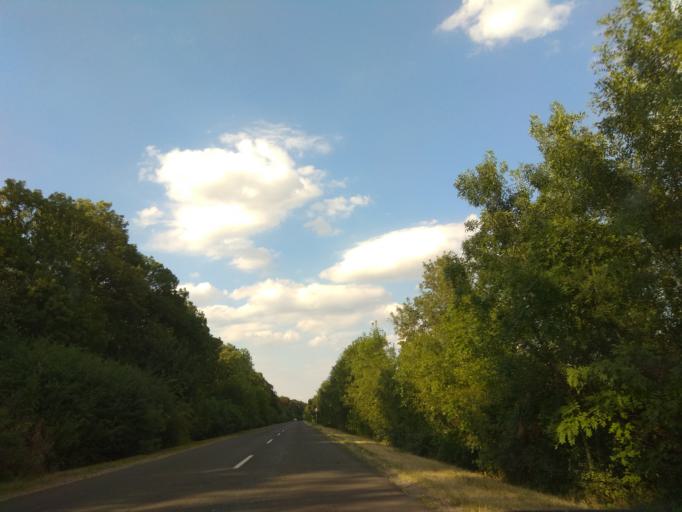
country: HU
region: Borsod-Abauj-Zemplen
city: Harsany
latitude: 47.9264
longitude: 20.7255
